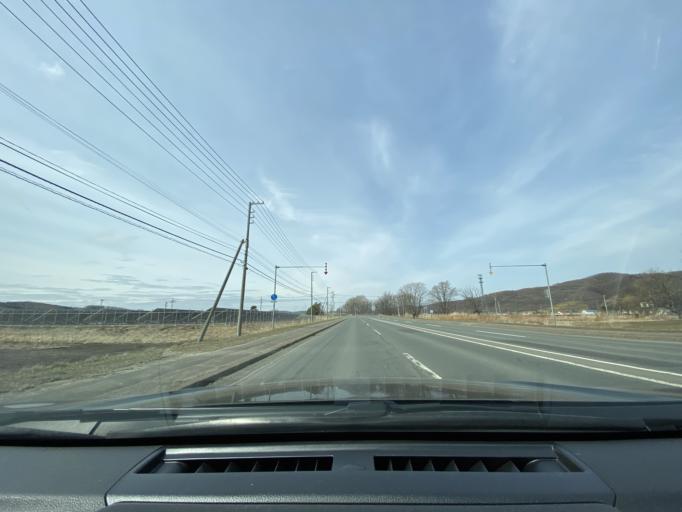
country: JP
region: Hokkaido
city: Kitami
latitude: 43.8017
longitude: 143.7889
